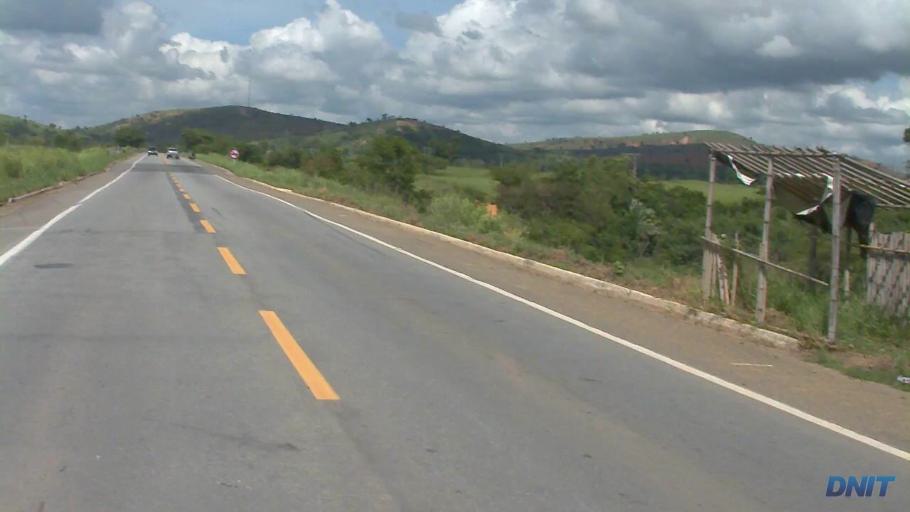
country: BR
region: Minas Gerais
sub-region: Governador Valadares
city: Governador Valadares
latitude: -19.0091
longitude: -42.1356
